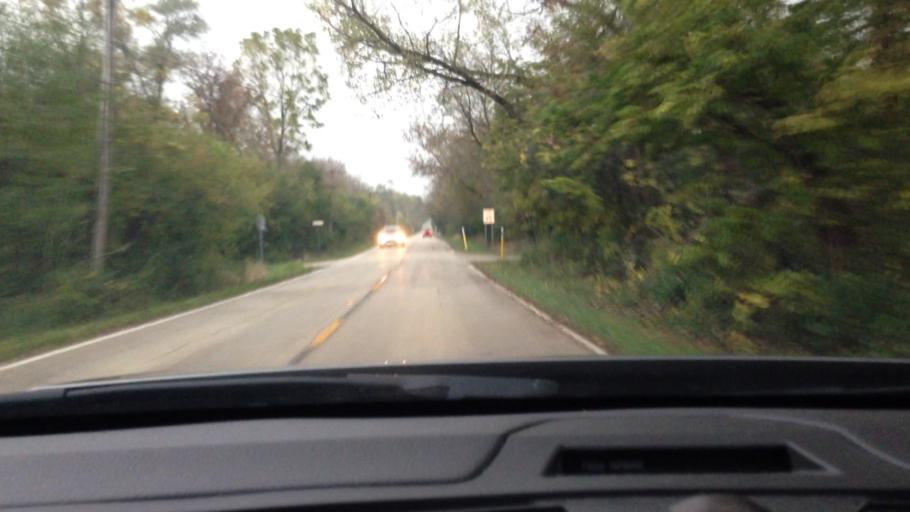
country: US
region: Illinois
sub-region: Cook County
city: Barrington Hills
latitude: 42.1007
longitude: -88.1946
